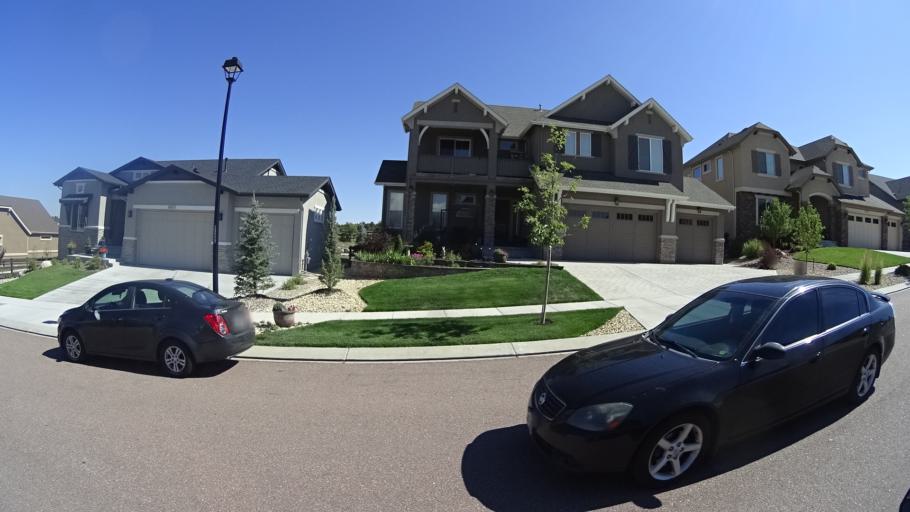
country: US
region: Colorado
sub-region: El Paso County
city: Black Forest
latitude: 38.9785
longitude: -104.7405
